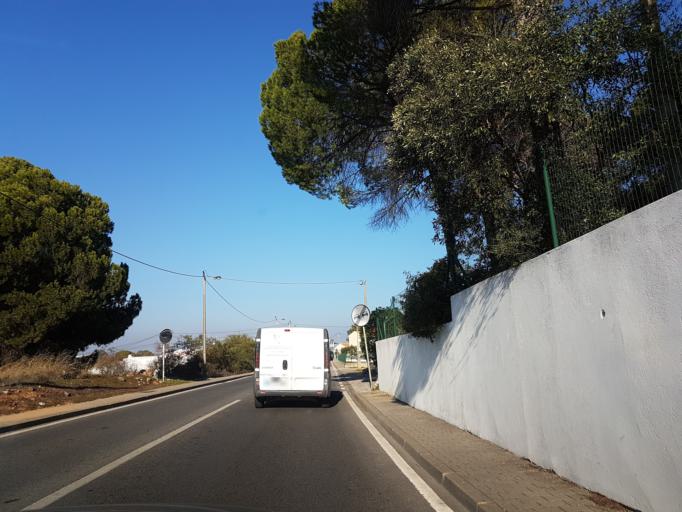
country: PT
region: Faro
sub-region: Albufeira
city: Ferreiras
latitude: 37.1052
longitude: -8.2146
